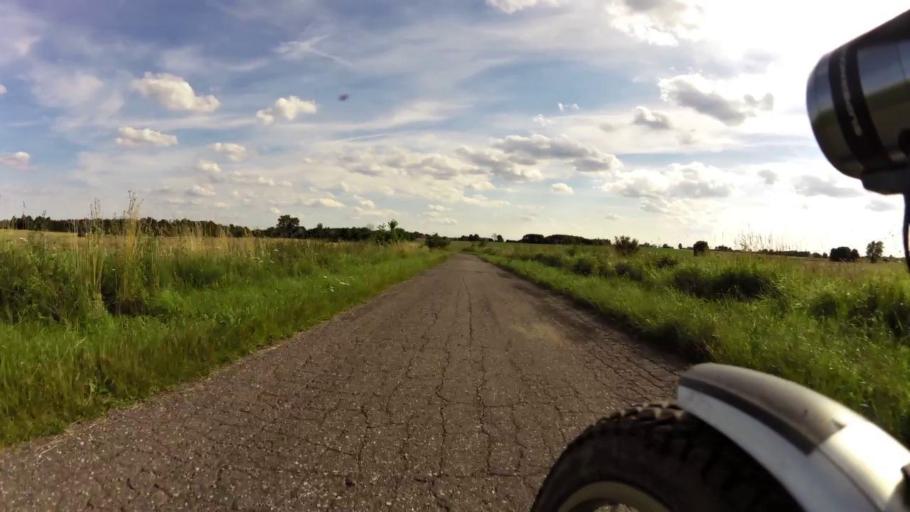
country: PL
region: West Pomeranian Voivodeship
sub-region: Powiat lobeski
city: Radowo Male
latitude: 53.5774
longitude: 15.4686
